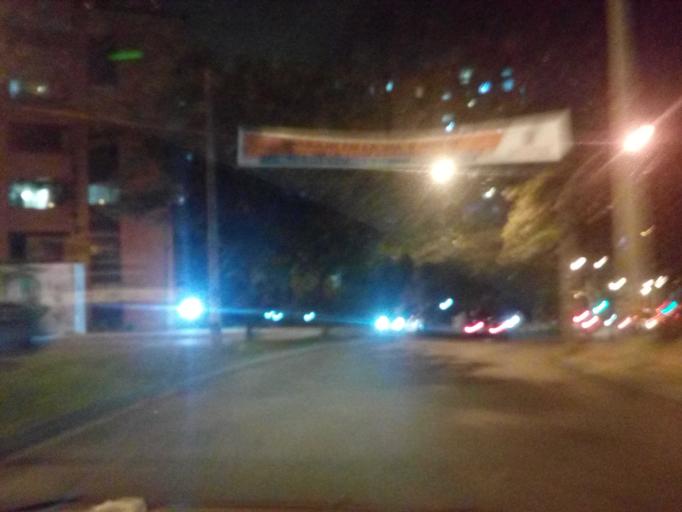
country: CO
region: Antioquia
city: Envigado
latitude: 6.1966
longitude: -75.5753
